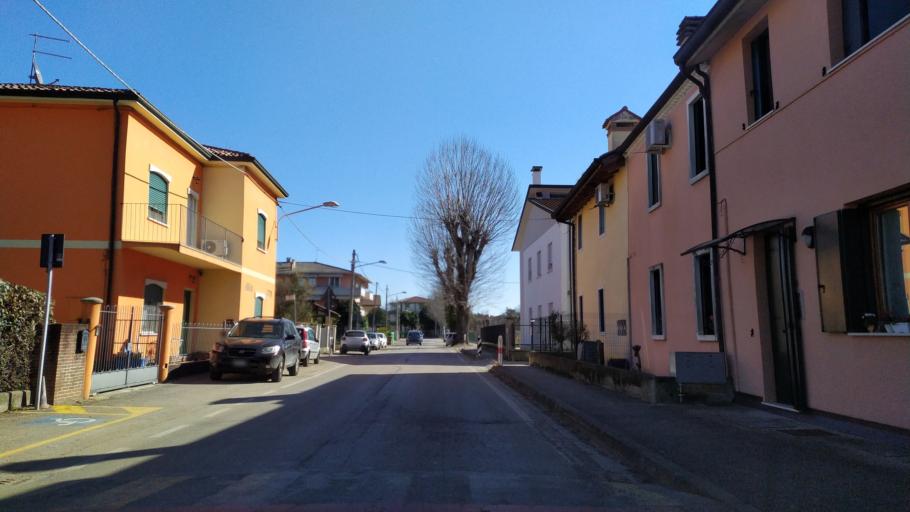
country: IT
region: Veneto
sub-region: Provincia di Vicenza
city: Monticello Conte Otto
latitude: 45.5905
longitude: 11.5529
